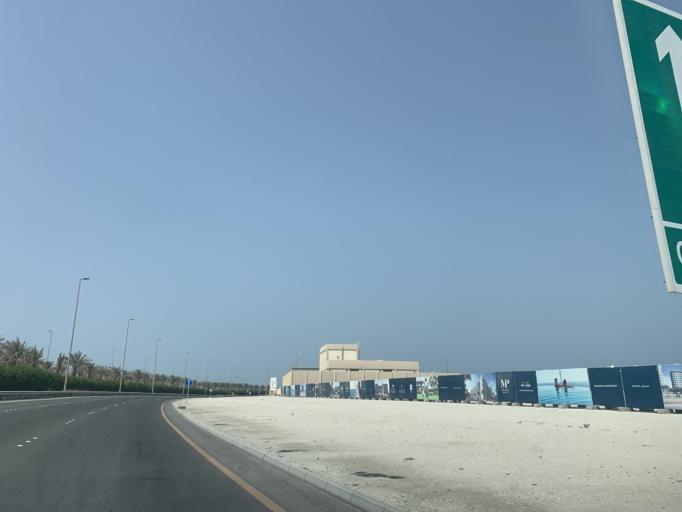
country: BH
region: Muharraq
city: Al Muharraq
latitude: 26.3092
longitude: 50.6405
